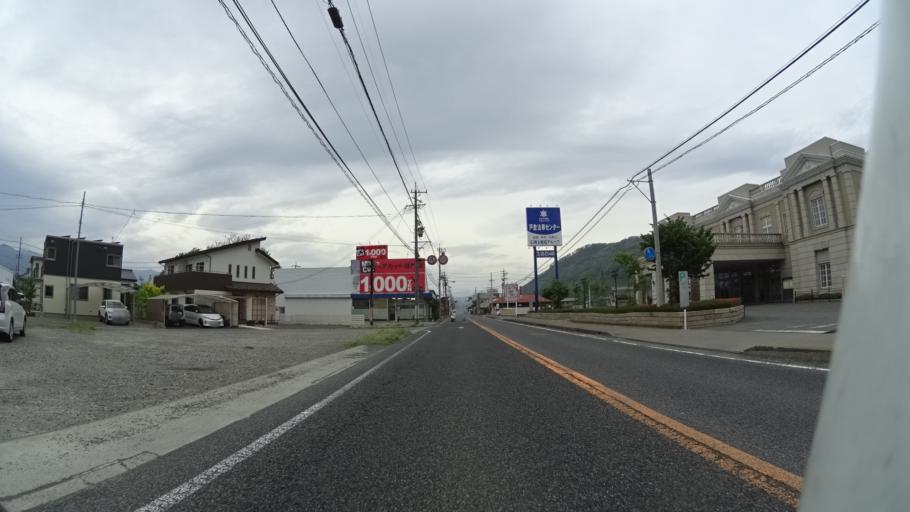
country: JP
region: Nagano
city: Nagano-shi
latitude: 36.5005
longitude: 138.1462
